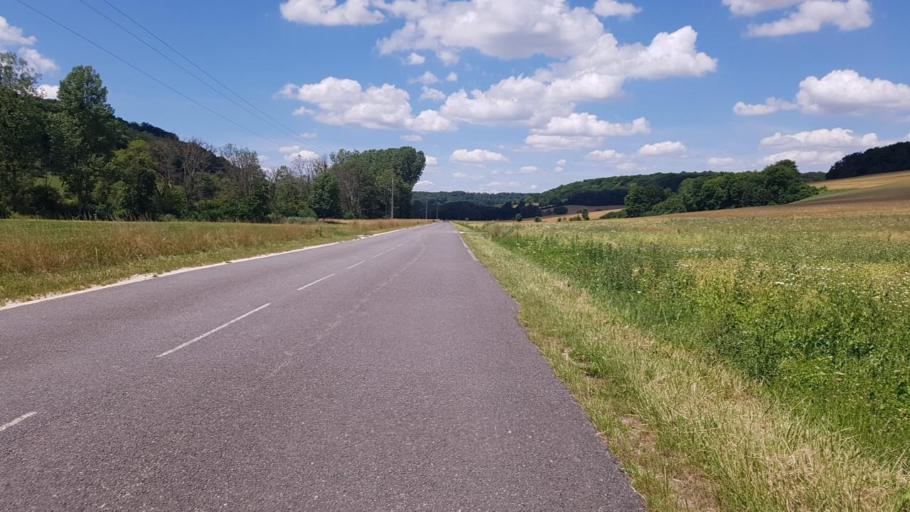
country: FR
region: Lorraine
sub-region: Departement de la Meuse
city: Ligny-en-Barrois
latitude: 48.6420
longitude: 5.4366
